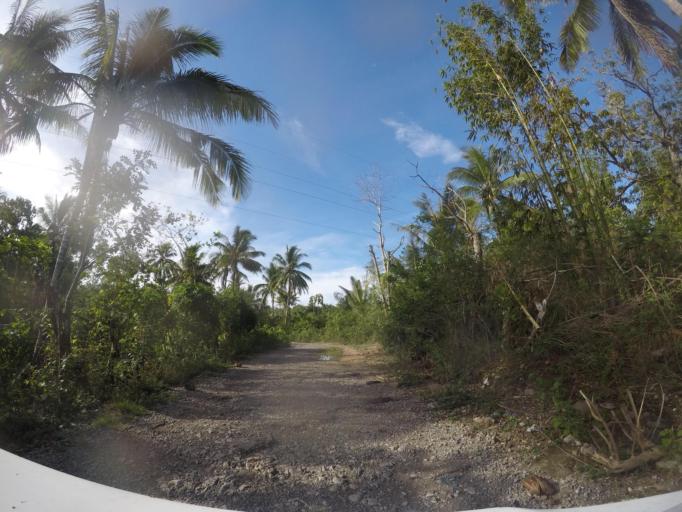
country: TL
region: Baucau
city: Baucau
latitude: -8.4925
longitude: 126.4538
